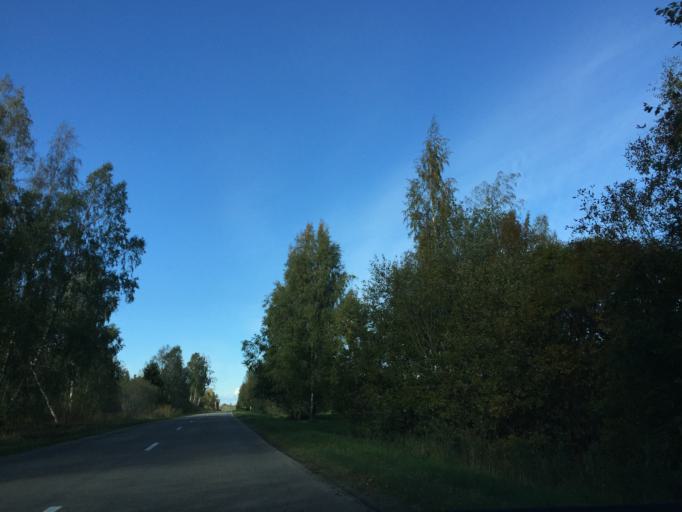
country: LV
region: Rojas
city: Roja
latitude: 57.4339
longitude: 22.9095
